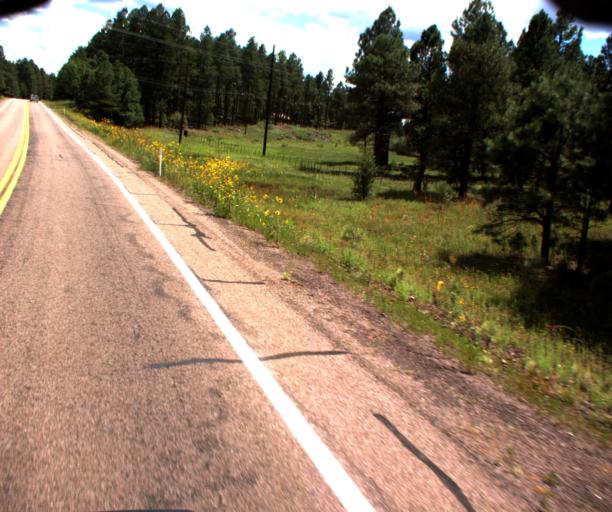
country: US
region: Arizona
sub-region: Navajo County
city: Pinetop-Lakeside
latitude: 34.0790
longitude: -109.8679
